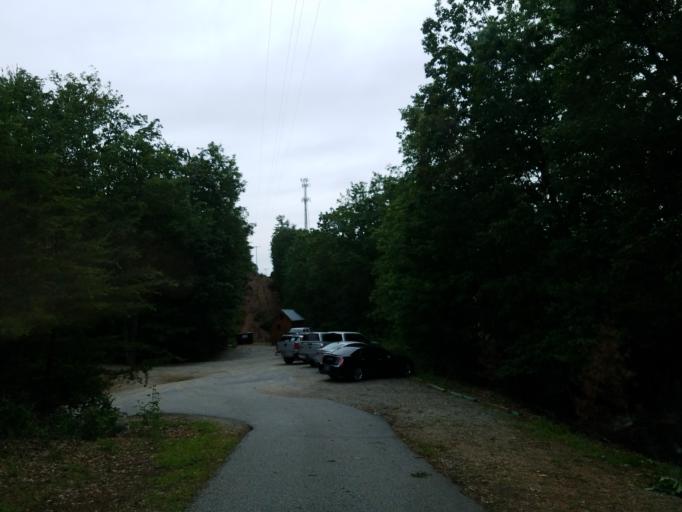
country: US
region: Georgia
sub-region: Lumpkin County
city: Dahlonega
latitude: 34.6139
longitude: -83.9649
